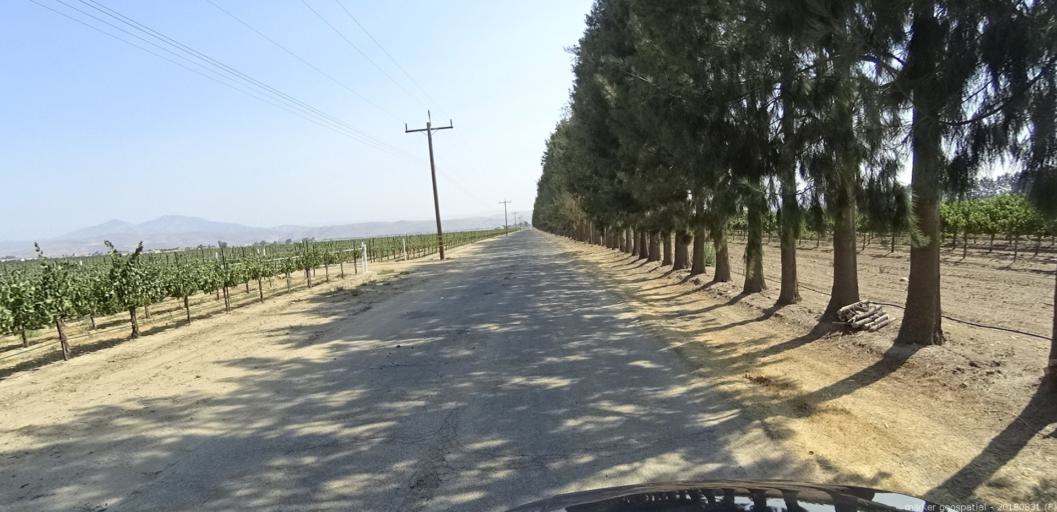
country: US
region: California
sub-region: Monterey County
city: Greenfield
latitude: 36.3032
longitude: -121.2393
